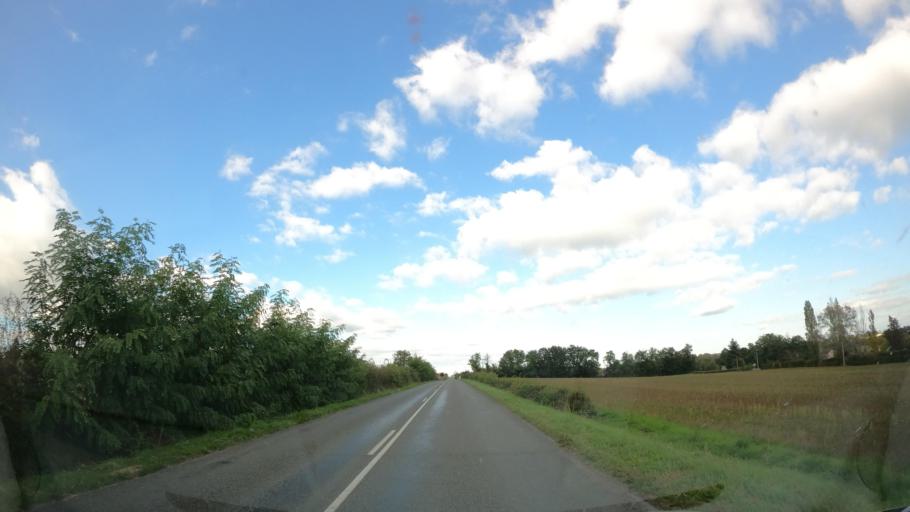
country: FR
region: Auvergne
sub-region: Departement de l'Allier
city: Dompierre-sur-Besbre
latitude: 46.5053
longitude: 3.6702
